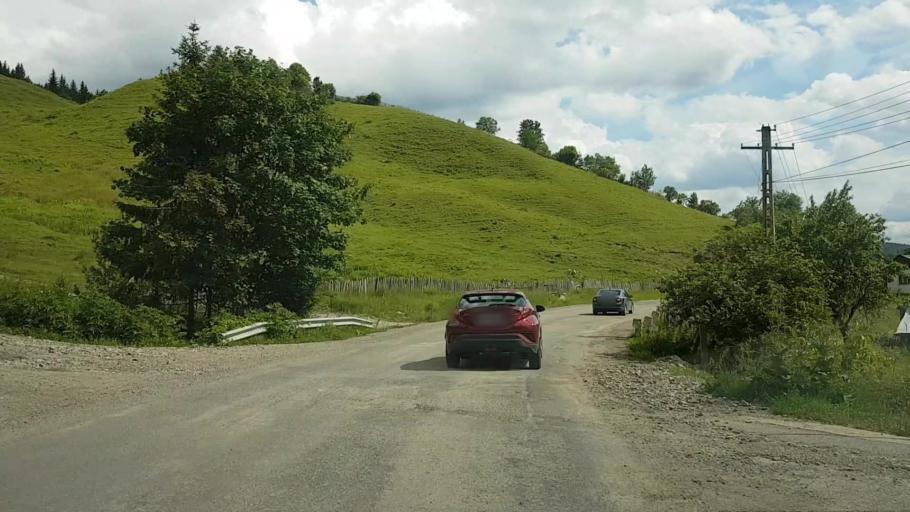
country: RO
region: Neamt
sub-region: Comuna Bicaz
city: Dodeni
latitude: 47.0042
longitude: 26.0982
